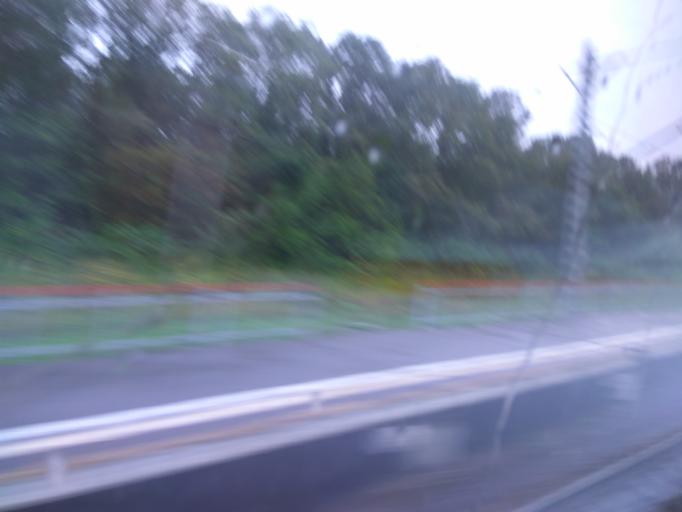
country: RU
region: Moskovskaya
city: Ozherel'ye
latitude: 54.8312
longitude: 38.2425
